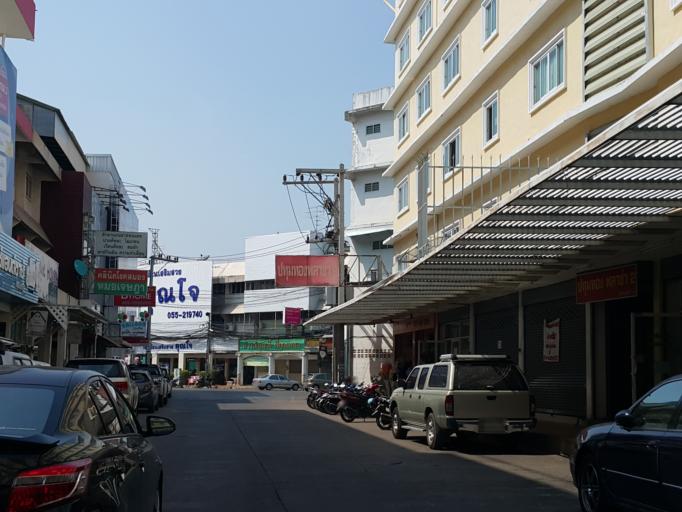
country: TH
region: Phitsanulok
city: Phitsanulok
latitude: 16.8101
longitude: 100.2607
